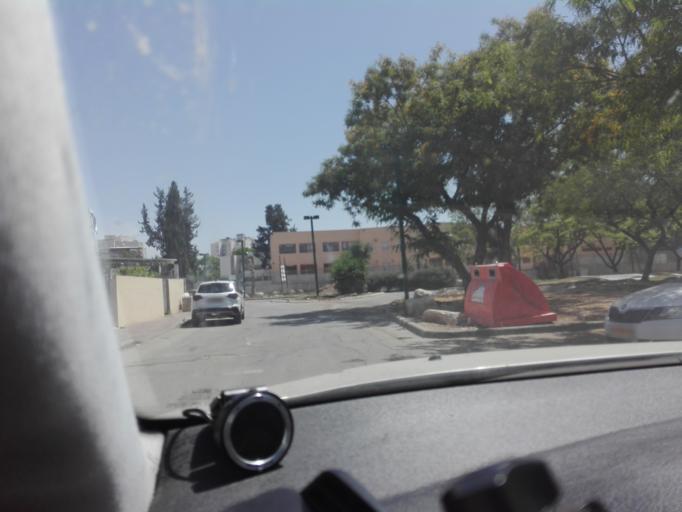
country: IL
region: Central District
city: Bene 'Ayish
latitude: 31.7322
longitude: 34.7451
